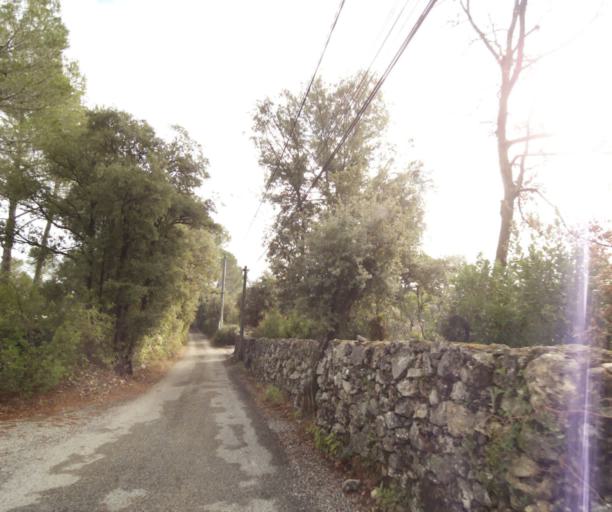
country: FR
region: Provence-Alpes-Cote d'Azur
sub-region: Departement du Var
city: Trans-en-Provence
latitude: 43.5046
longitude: 6.4990
